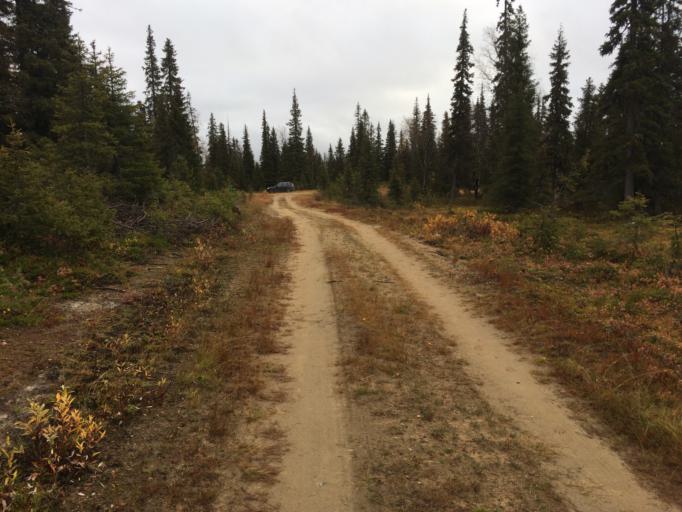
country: FI
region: Lapland
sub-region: Itae-Lappi
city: Salla
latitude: 66.6683
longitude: 28.5893
